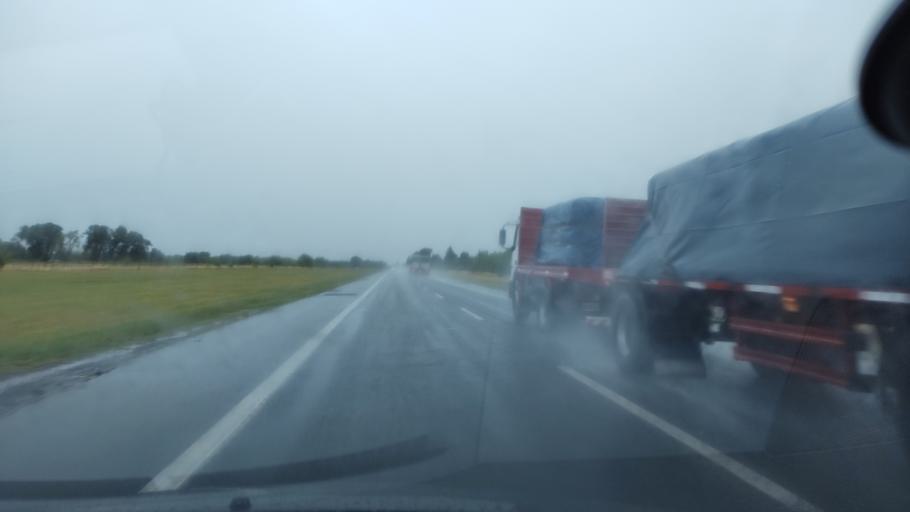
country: AR
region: Buenos Aires
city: Canuelas
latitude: -35.0613
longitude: -58.8091
